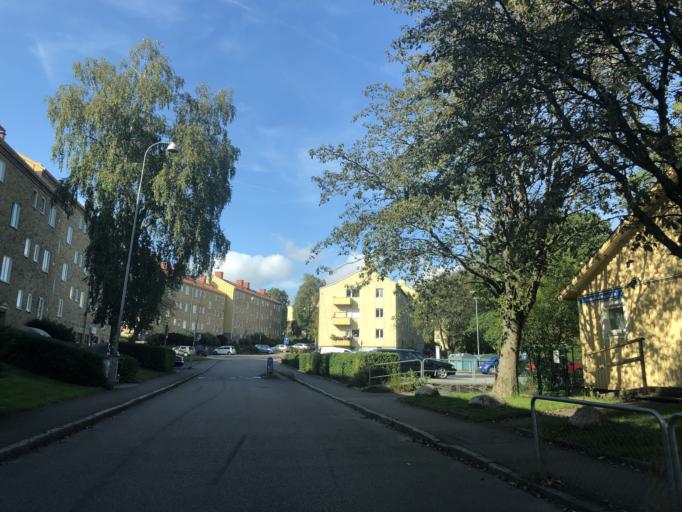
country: SE
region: Vaestra Goetaland
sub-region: Goteborg
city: Majorna
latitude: 57.6770
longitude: 11.9252
